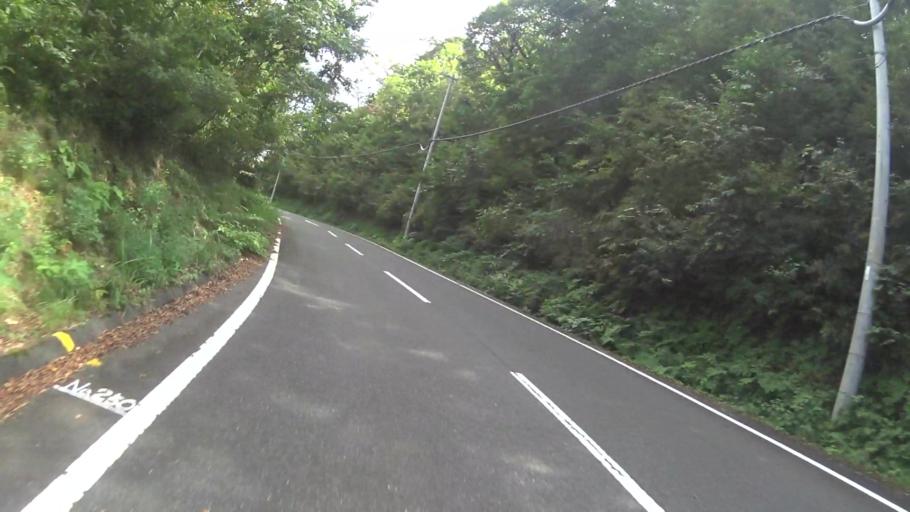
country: JP
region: Kyoto
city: Miyazu
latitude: 35.7260
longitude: 135.1867
